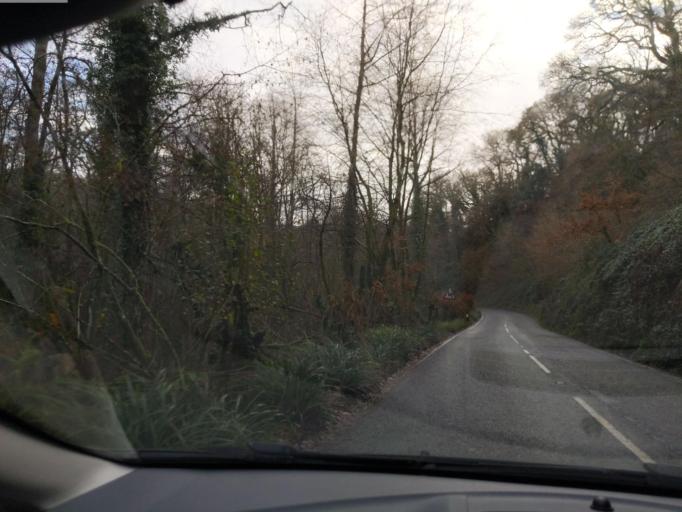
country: GB
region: England
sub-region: Cornwall
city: Looe
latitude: 50.3853
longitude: -4.3902
